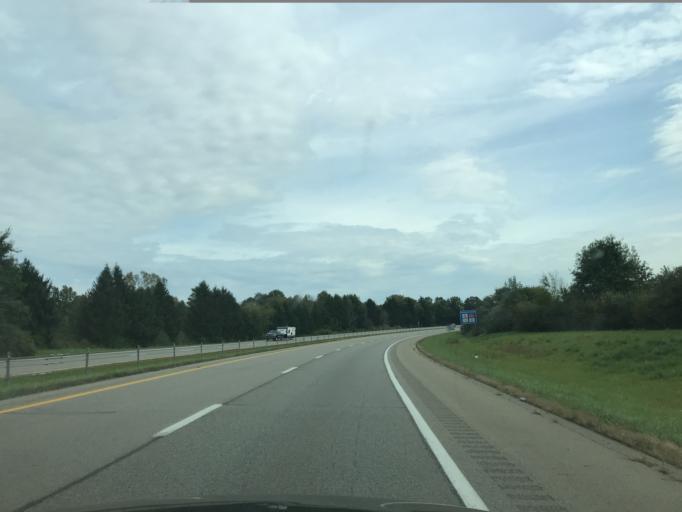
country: US
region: Ohio
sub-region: Trumbull County
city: Champion Heights
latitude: 41.2746
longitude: -80.8607
